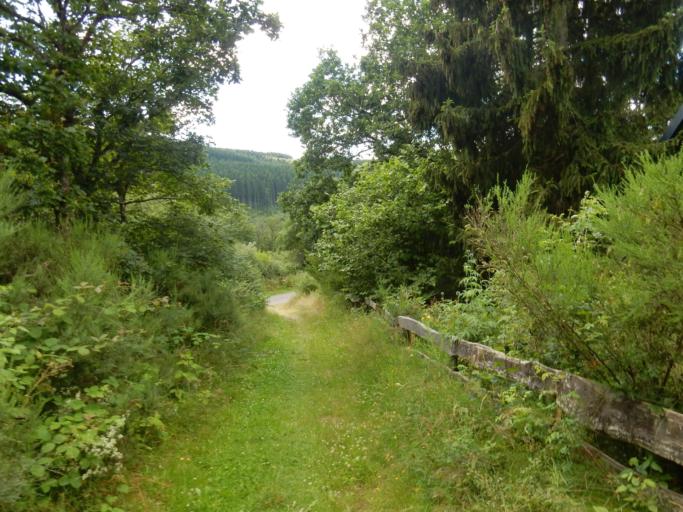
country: LU
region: Diekirch
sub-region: Canton de Wiltz
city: Wilwerwiltz
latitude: 49.9511
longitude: 6.0233
